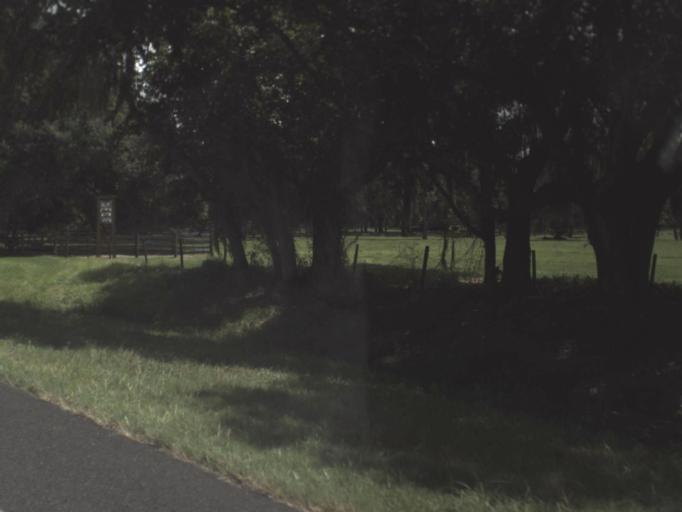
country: US
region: Florida
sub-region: Polk County
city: Alturas
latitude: 27.9097
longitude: -81.6820
